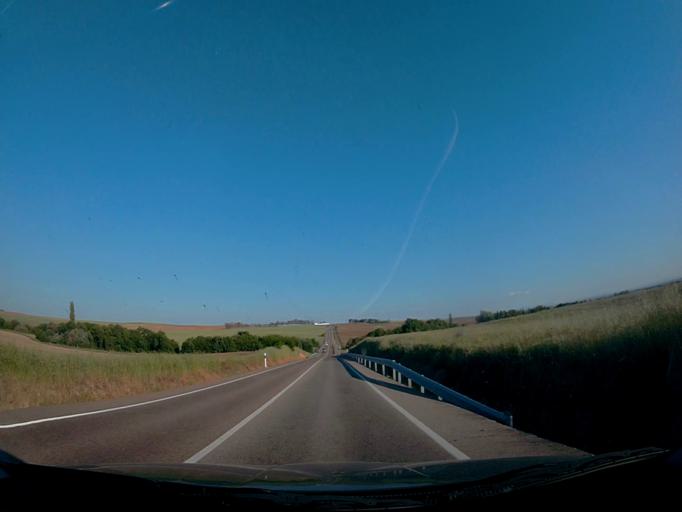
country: ES
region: Castille-La Mancha
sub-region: Province of Toledo
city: Hormigos
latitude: 40.1054
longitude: -4.3978
